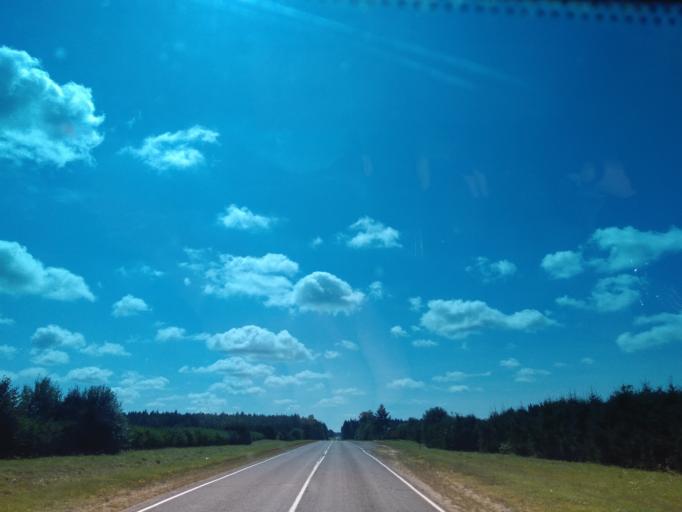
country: BY
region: Minsk
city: Uzda
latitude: 53.3371
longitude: 27.2293
